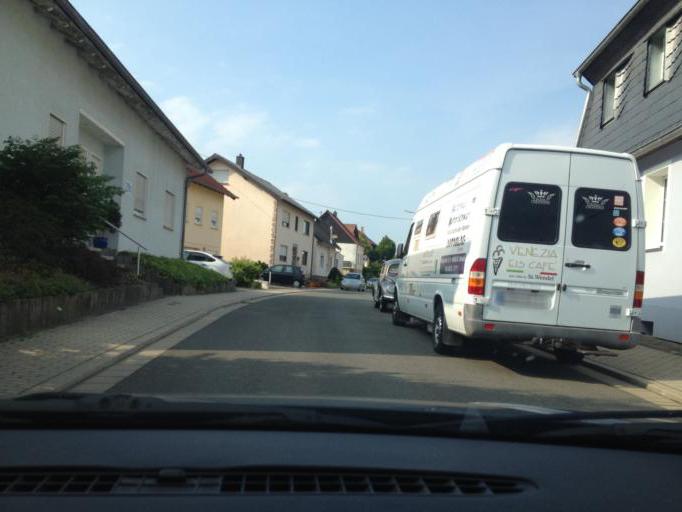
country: DE
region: Saarland
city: Namborn
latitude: 49.5254
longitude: 7.1413
